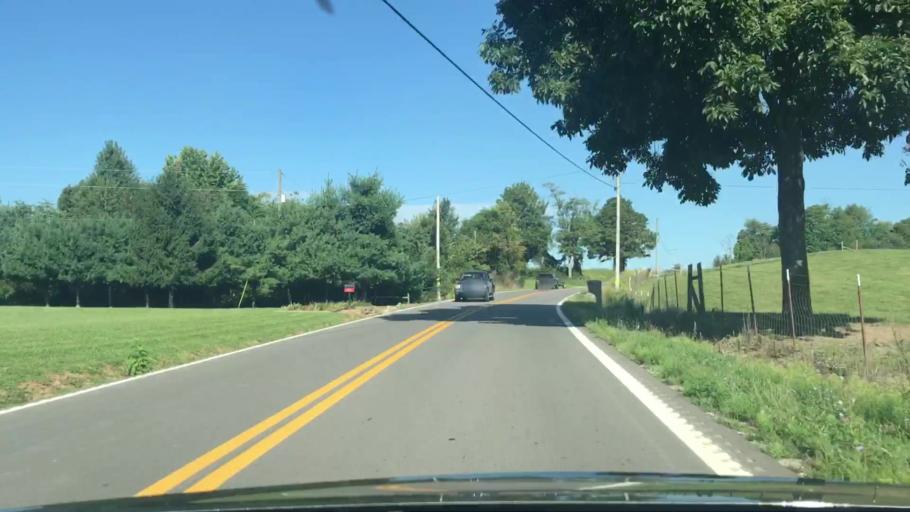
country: US
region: Tennessee
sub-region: Pickett County
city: Byrdstown
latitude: 36.6188
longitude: -85.0806
